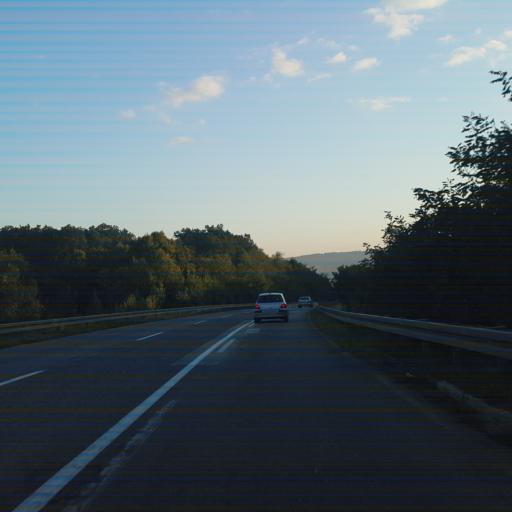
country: RS
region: Central Serbia
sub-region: Zajecarski Okrug
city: Zajecar
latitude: 44.0748
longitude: 22.3339
